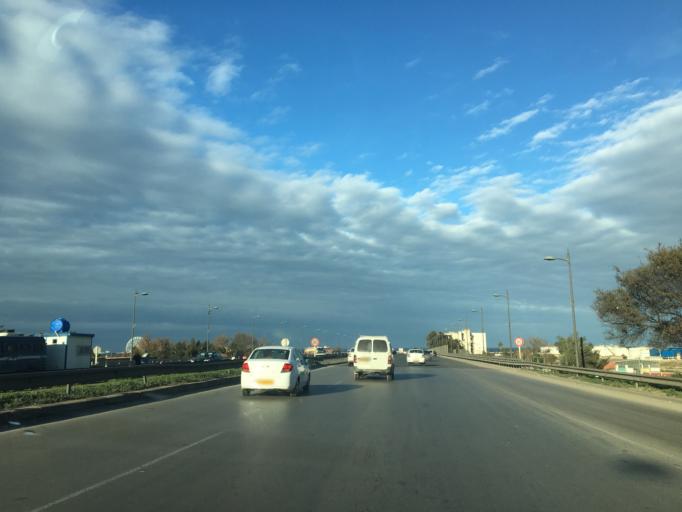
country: DZ
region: Alger
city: Bab Ezzouar
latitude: 36.7339
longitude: 3.1200
